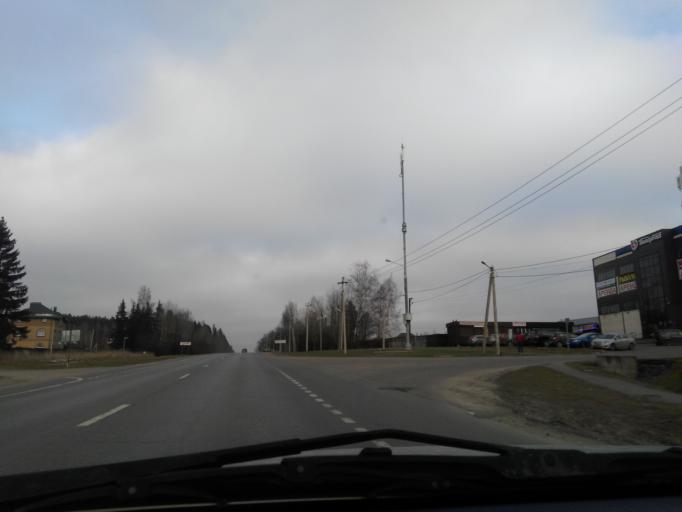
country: RU
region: Moskovskaya
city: Troitsk
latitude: 55.3082
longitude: 37.1465
